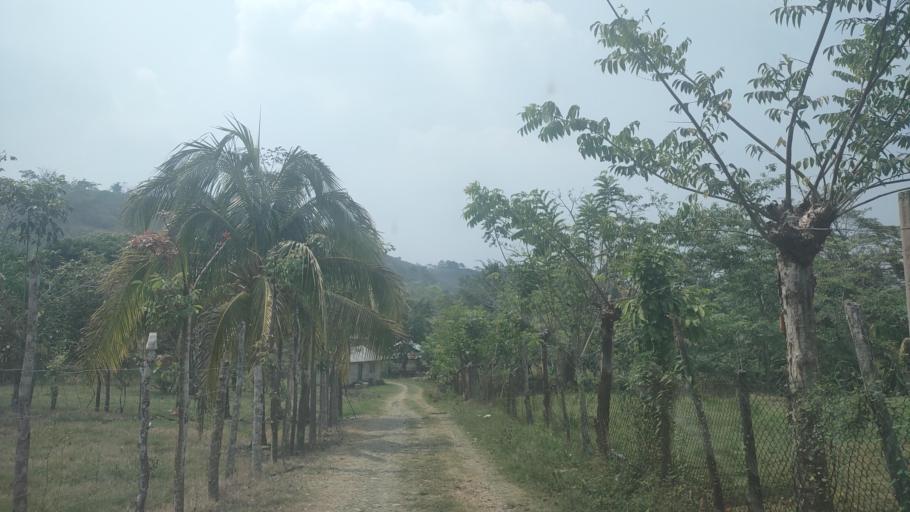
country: MX
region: Tabasco
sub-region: Huimanguillo
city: Francisco Rueda
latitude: 17.6669
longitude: -93.8857
